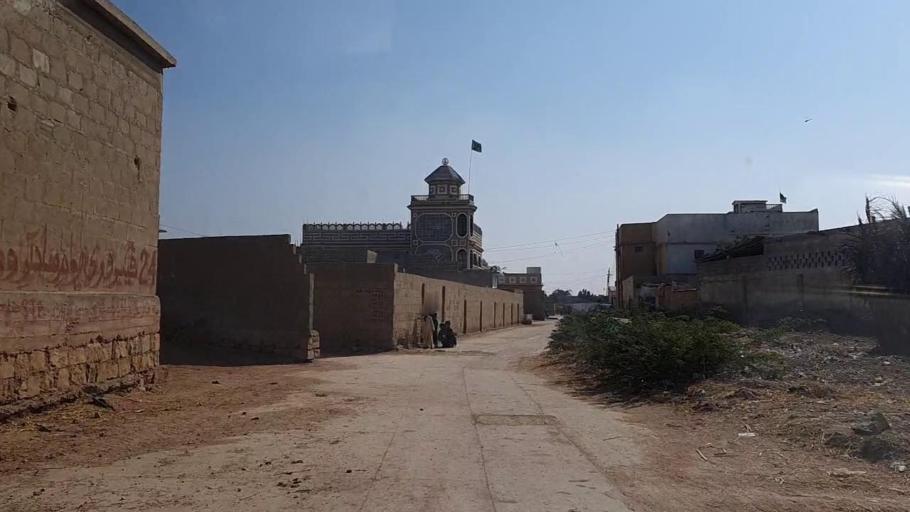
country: PK
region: Sindh
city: Thatta
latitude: 24.7950
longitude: 67.9599
